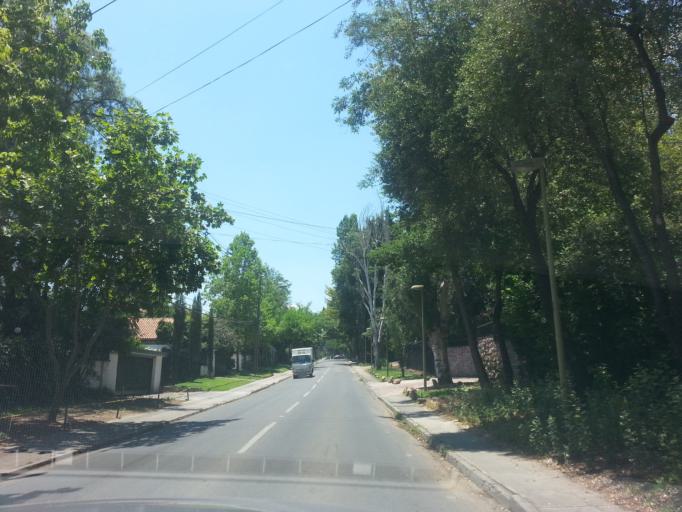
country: CL
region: Santiago Metropolitan
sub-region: Provincia de Santiago
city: Villa Presidente Frei, Nunoa, Santiago, Chile
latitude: -33.3924
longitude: -70.5293
